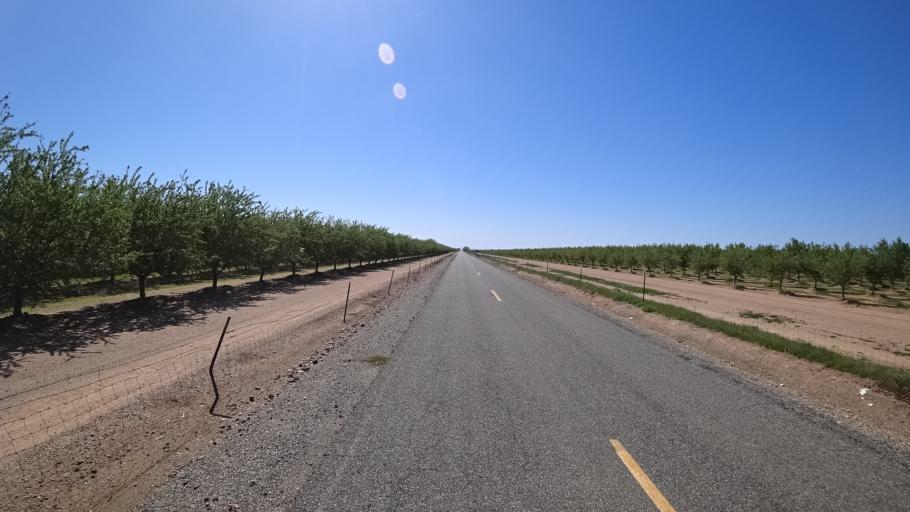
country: US
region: California
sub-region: Glenn County
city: Orland
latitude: 39.6572
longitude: -122.2532
